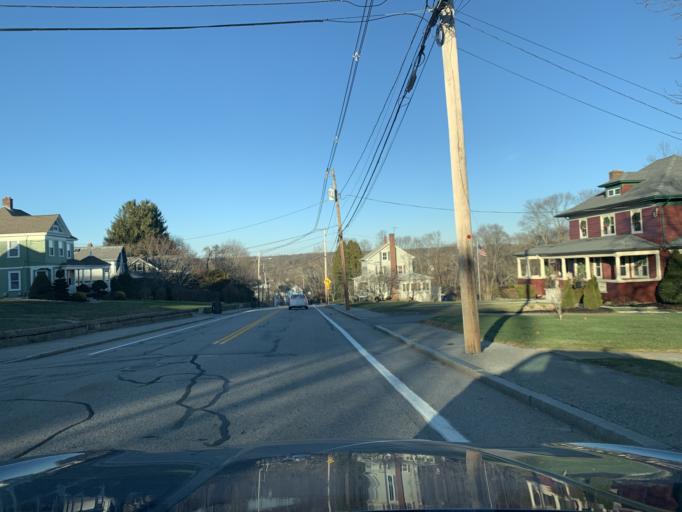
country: US
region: Rhode Island
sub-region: Kent County
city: West Warwick
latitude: 41.7173
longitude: -71.5332
